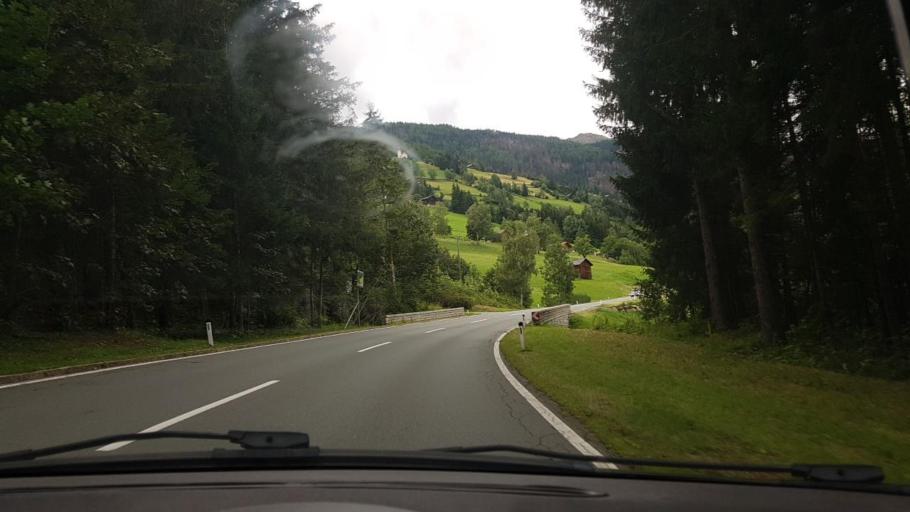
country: AT
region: Carinthia
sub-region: Politischer Bezirk Spittal an der Drau
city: Winklern
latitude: 46.8646
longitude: 12.8708
